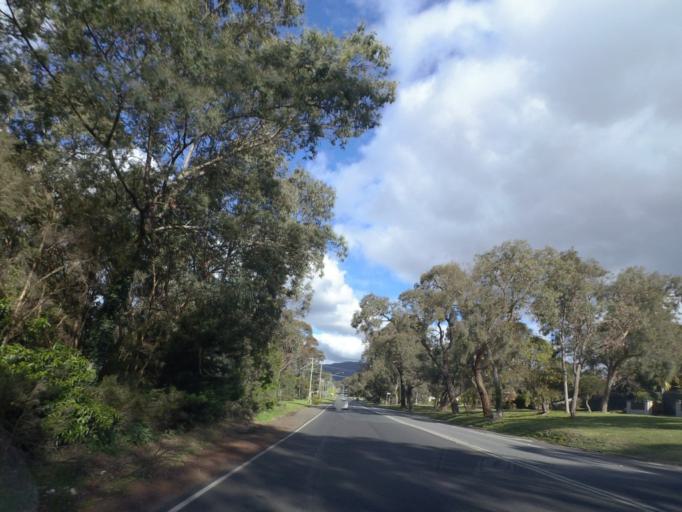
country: AU
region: Victoria
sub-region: Maroondah
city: Bayswater North
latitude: -37.8420
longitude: 145.2977
